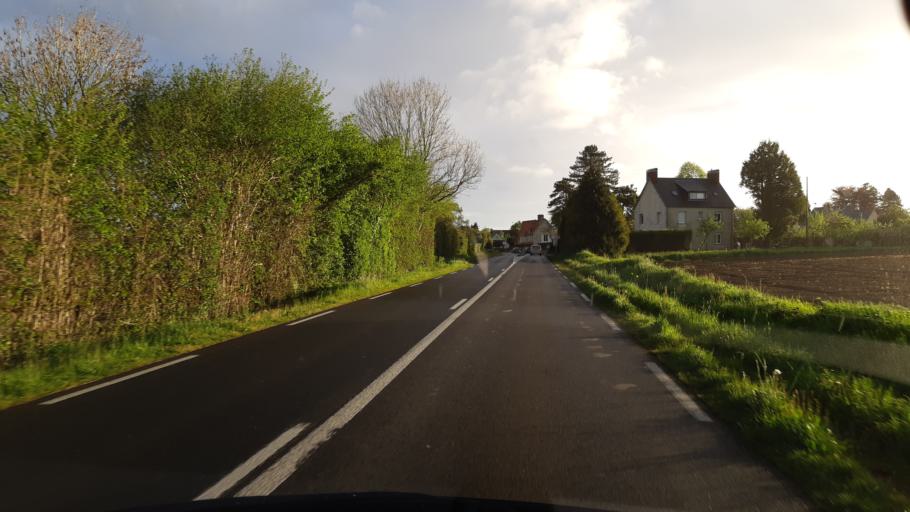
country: FR
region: Lower Normandy
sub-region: Departement de la Manche
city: Agneaux
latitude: 49.0435
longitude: -1.1290
